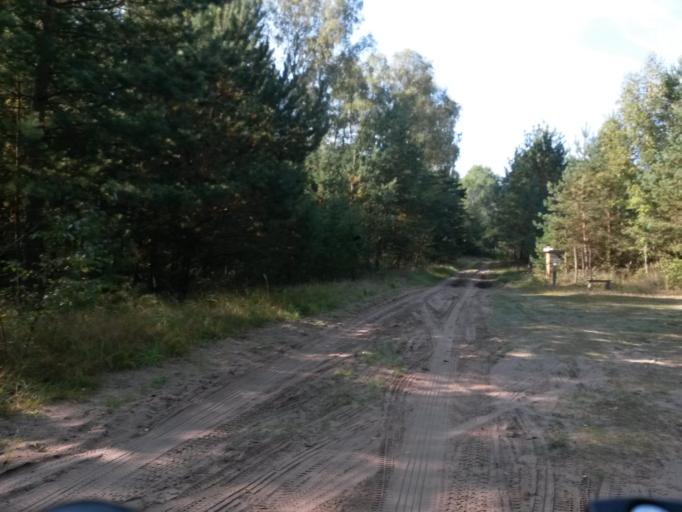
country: DE
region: Brandenburg
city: Templin
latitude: 53.0861
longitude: 13.4100
